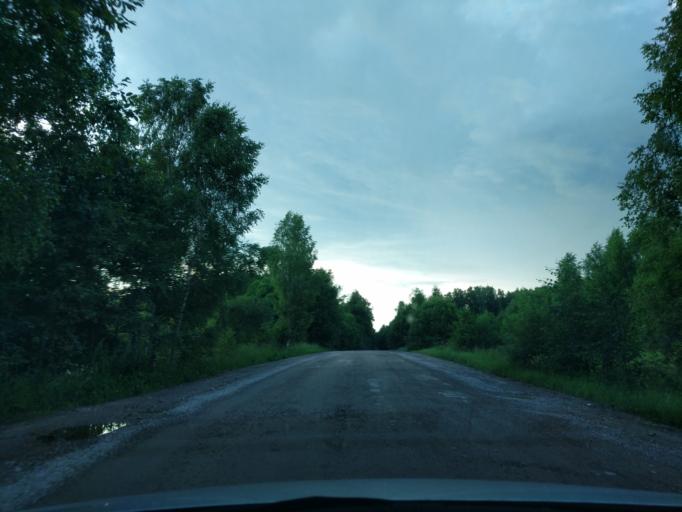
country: RU
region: Kaluga
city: Myatlevo
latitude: 54.8603
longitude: 35.5720
